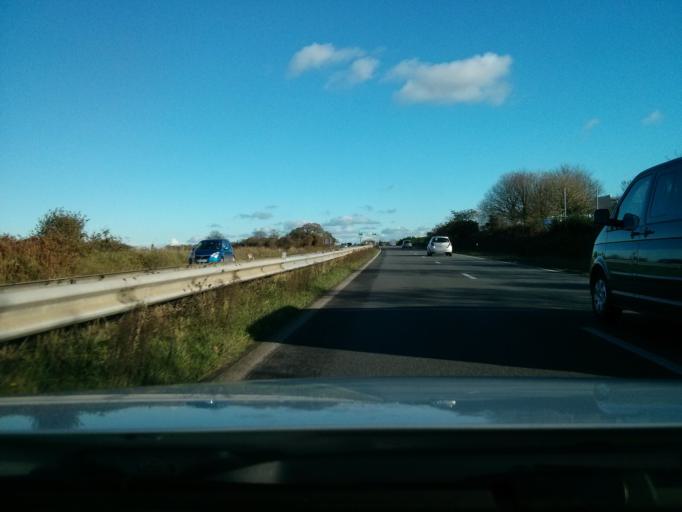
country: FR
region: Brittany
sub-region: Departement du Finistere
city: Gouesnou
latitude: 48.4331
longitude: -4.4534
